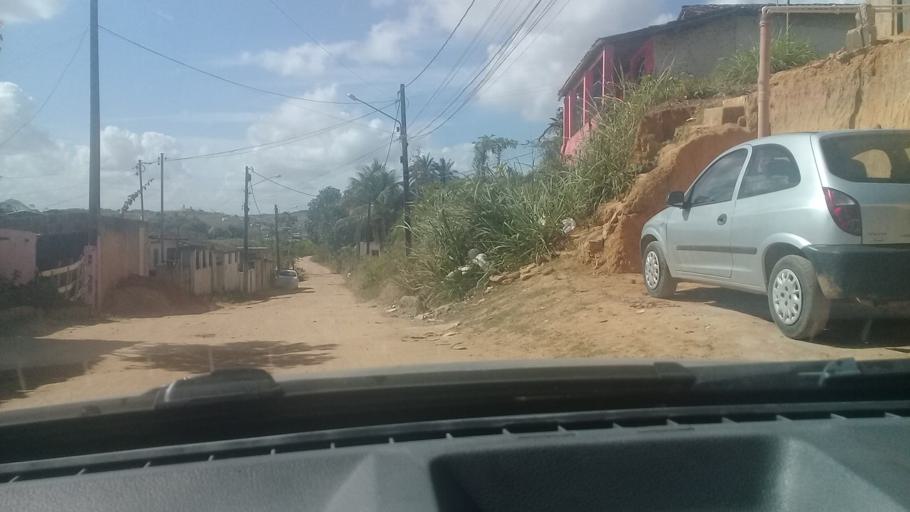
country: BR
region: Pernambuco
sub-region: Jaboatao Dos Guararapes
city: Jaboatao dos Guararapes
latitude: -8.0876
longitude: -35.0305
